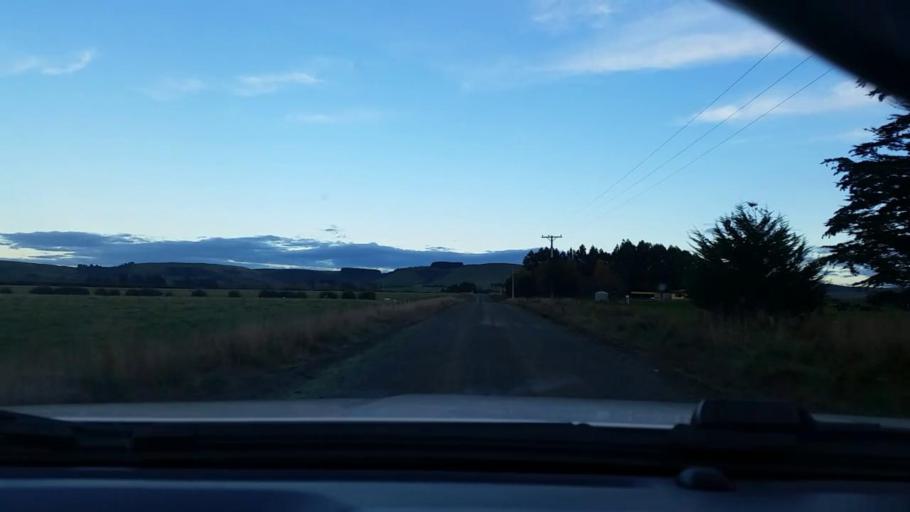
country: NZ
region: Southland
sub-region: Southland District
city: Winton
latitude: -46.1084
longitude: 168.4422
